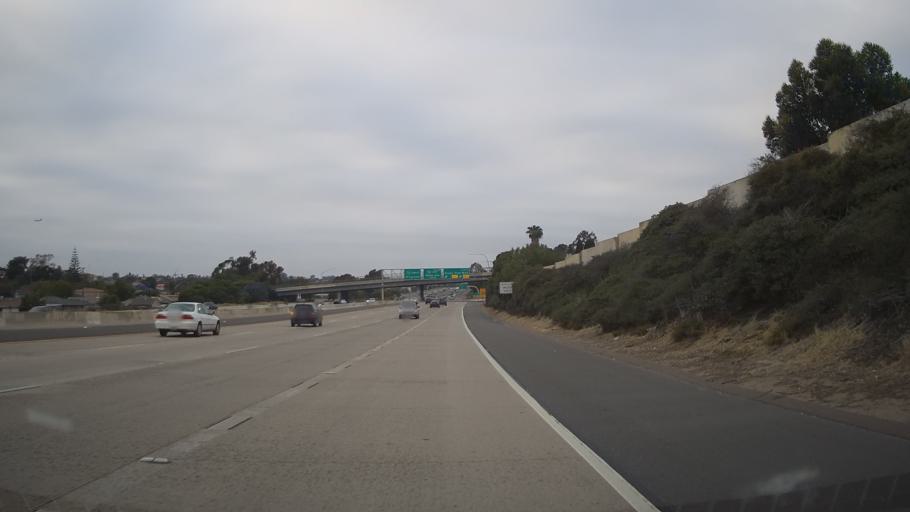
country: US
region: California
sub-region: San Diego County
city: National City
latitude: 32.6983
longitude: -117.1207
